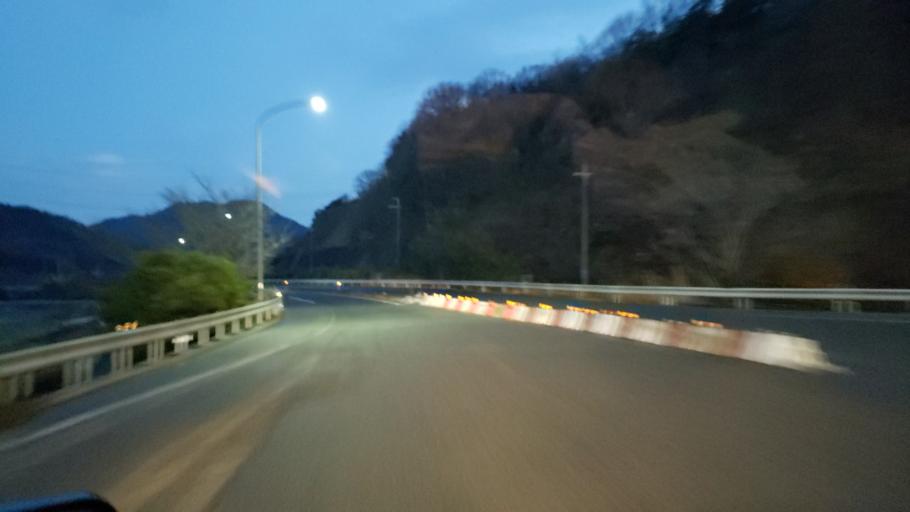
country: JP
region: Hyogo
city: Kakogawacho-honmachi
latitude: 34.8467
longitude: 134.8320
